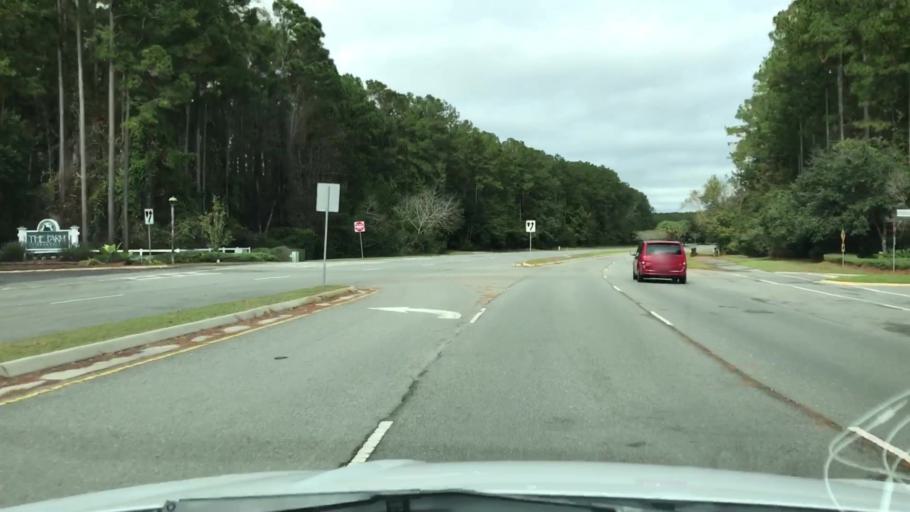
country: US
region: South Carolina
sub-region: Beaufort County
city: Bluffton
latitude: 32.2381
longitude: -80.9035
